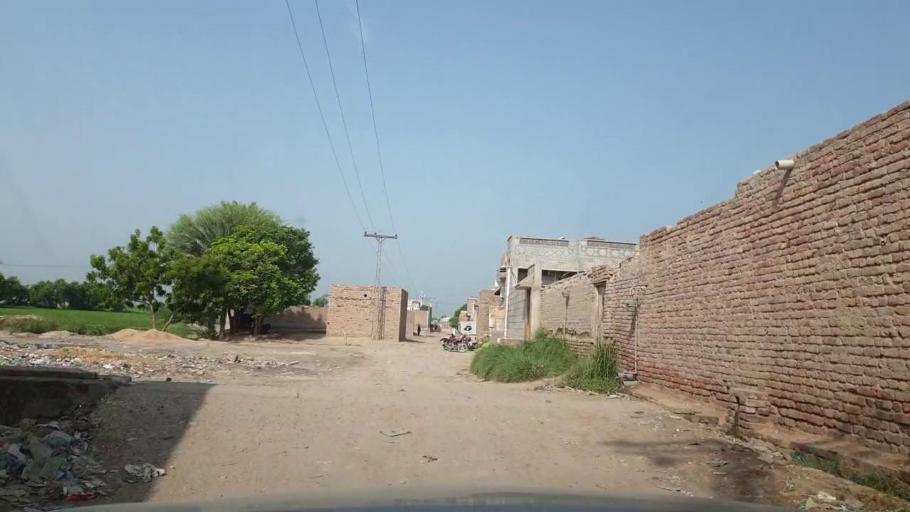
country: PK
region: Sindh
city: Bagarji
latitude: 27.8080
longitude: 68.7507
